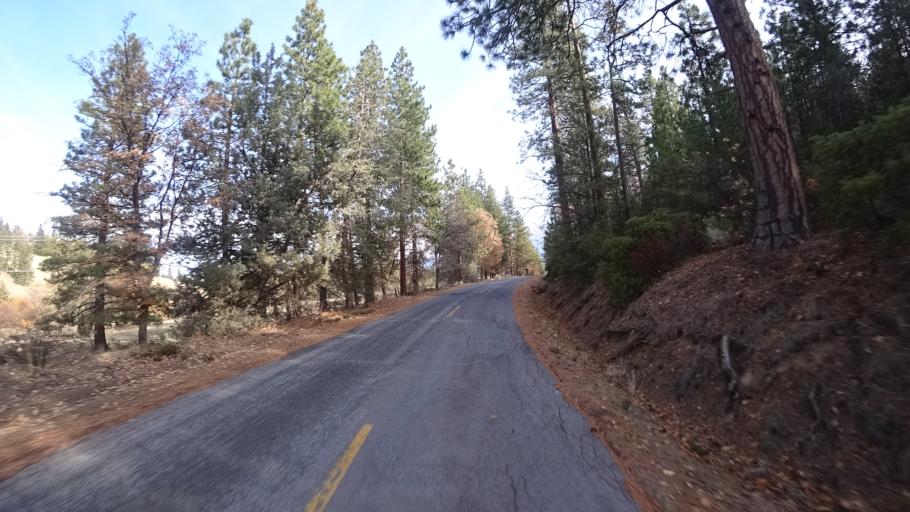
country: US
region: California
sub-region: Siskiyou County
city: Weed
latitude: 41.4673
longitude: -122.4088
